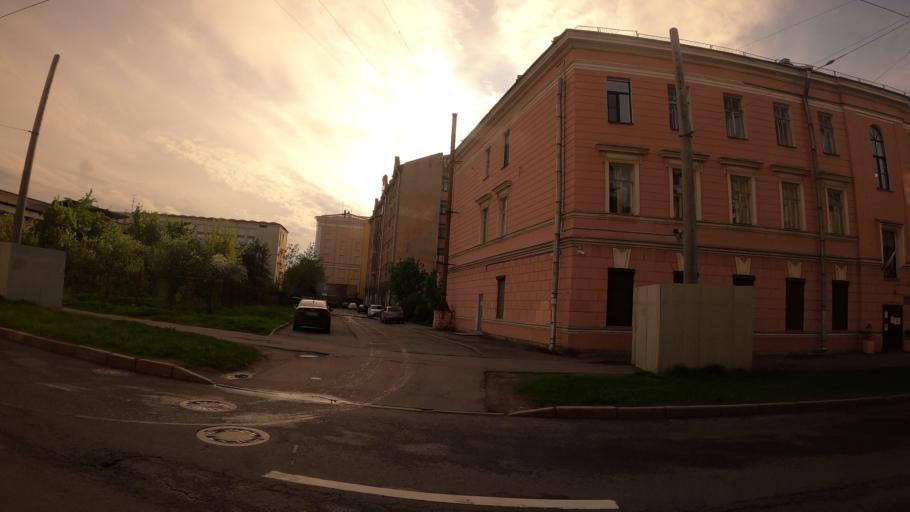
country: RU
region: St.-Petersburg
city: Vasyl'evsky Ostrov
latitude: 59.9317
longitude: 30.2488
